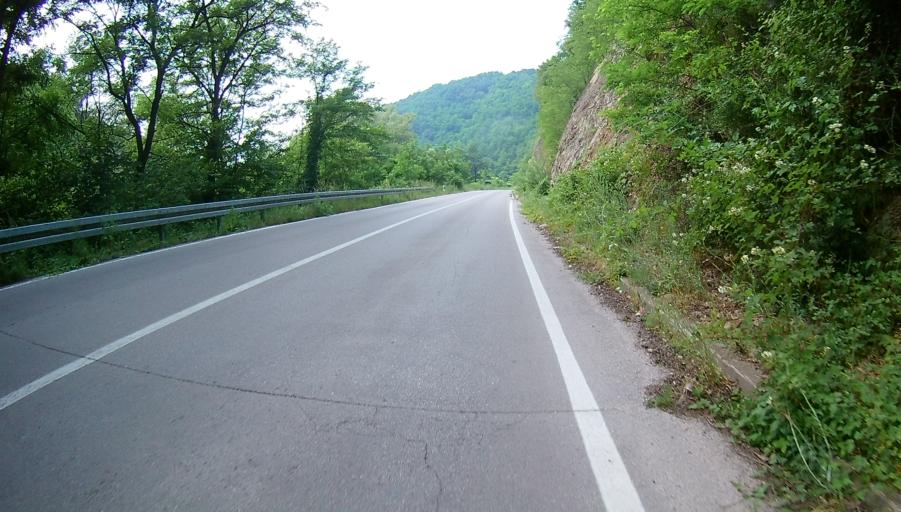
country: RS
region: Central Serbia
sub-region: Nisavski Okrug
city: Gadzin Han
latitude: 43.1702
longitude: 22.0698
